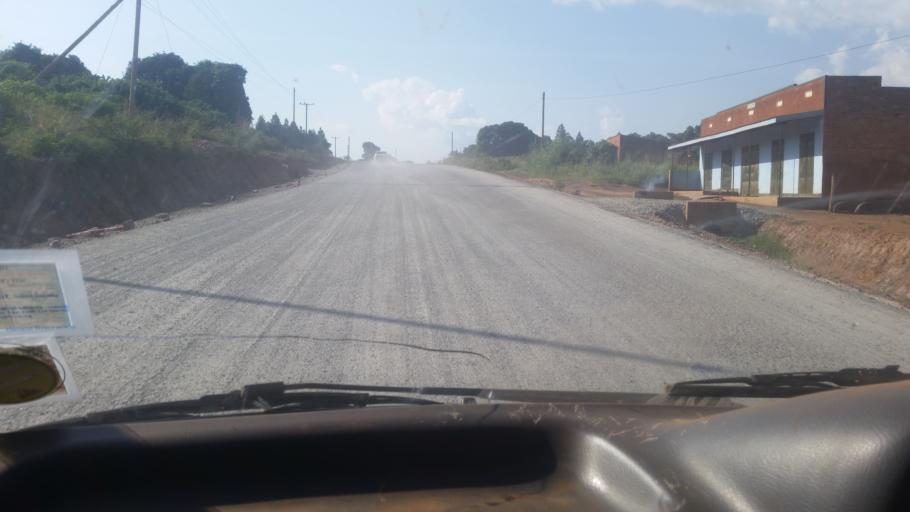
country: UG
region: Western Region
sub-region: Hoima District
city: Hoima
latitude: 1.3923
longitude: 31.3320
